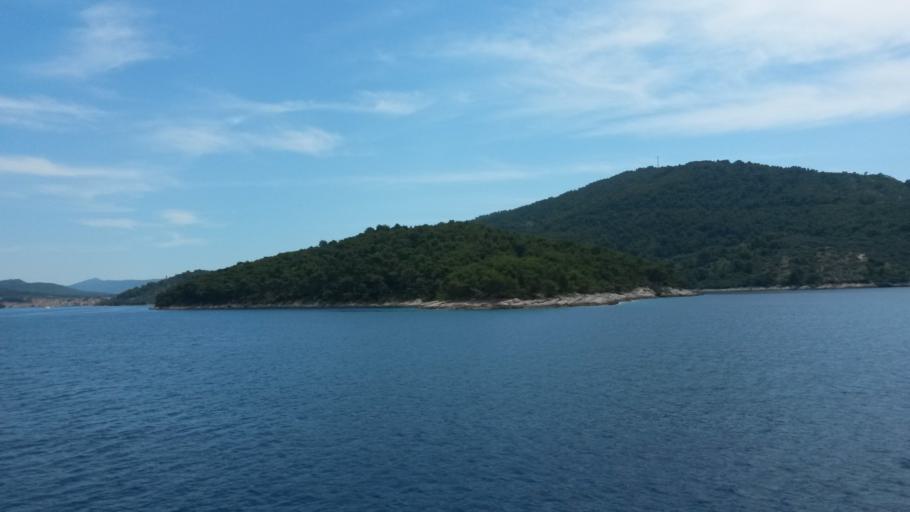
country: HR
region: Dubrovacko-Neretvanska
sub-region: Grad Dubrovnik
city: Vela Luka
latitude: 42.9641
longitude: 16.6745
